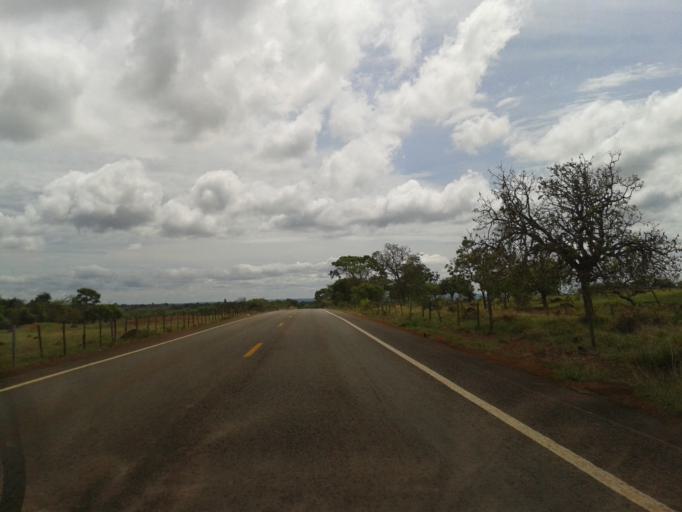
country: BR
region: Goias
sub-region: Buriti Alegre
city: Buriti Alegre
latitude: -18.1282
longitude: -49.1429
